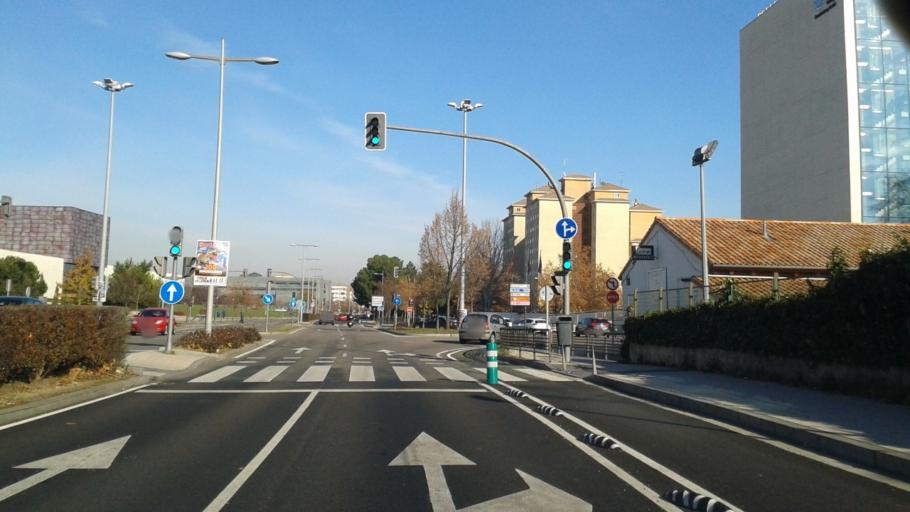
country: ES
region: Castille and Leon
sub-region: Provincia de Valladolid
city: Valladolid
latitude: 41.6407
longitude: -4.7447
